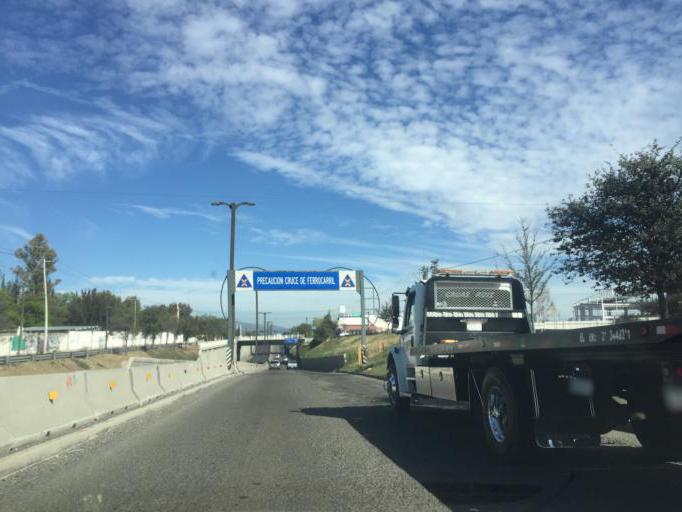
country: MX
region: Queretaro
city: San Juan del Rio
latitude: 20.3737
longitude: -99.9865
